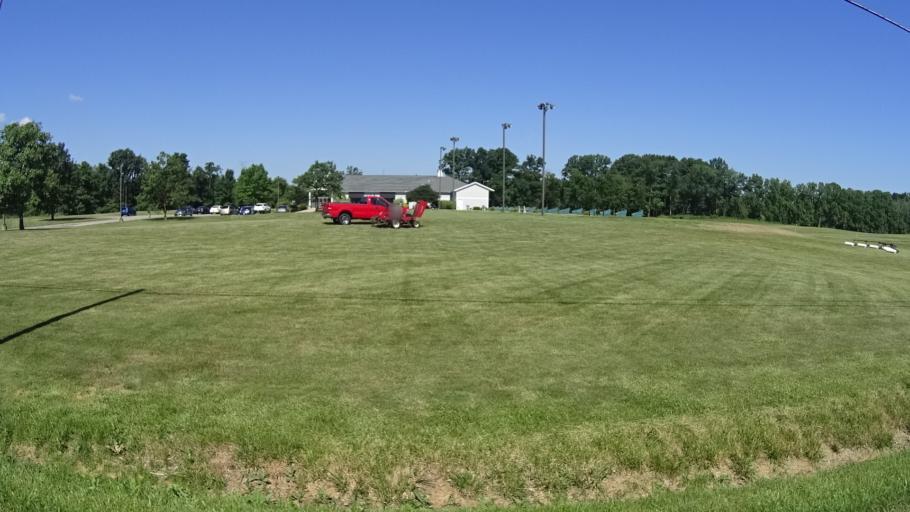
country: US
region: Ohio
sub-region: Erie County
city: Huron
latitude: 41.3671
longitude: -82.5711
